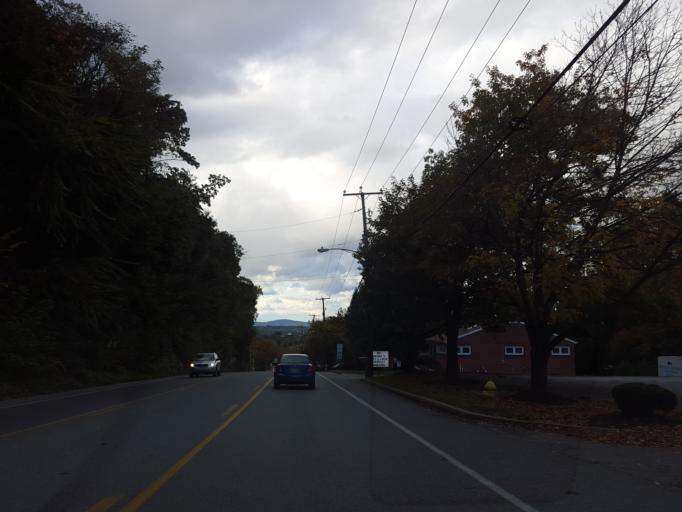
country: US
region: Pennsylvania
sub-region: York County
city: Valley View
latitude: 39.9466
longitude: -76.7097
